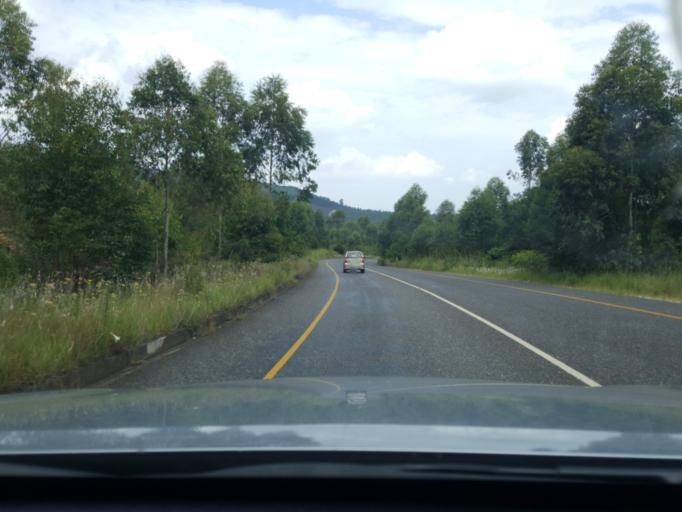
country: ZA
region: Mpumalanga
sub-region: Ehlanzeni District
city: White River
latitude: -25.1744
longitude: 30.8703
